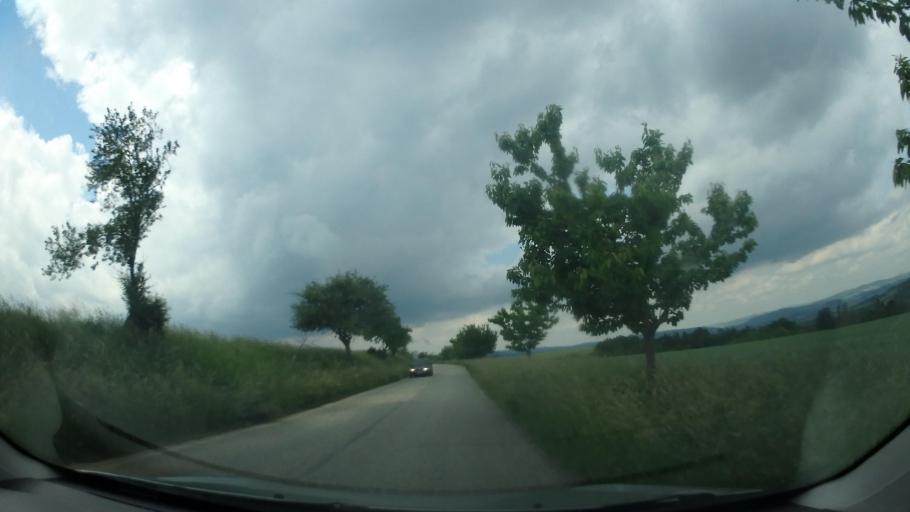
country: CZ
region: South Moravian
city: Boritov
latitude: 49.4544
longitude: 16.6014
